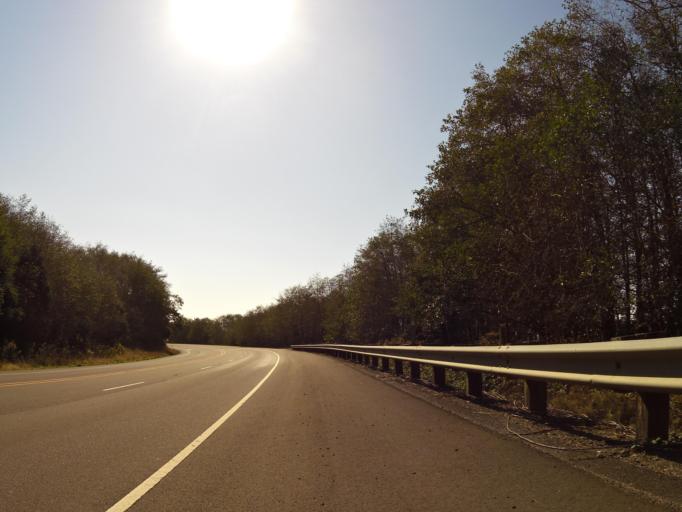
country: US
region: Oregon
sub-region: Tillamook County
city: Pacific City
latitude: 45.1456
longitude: -123.9678
